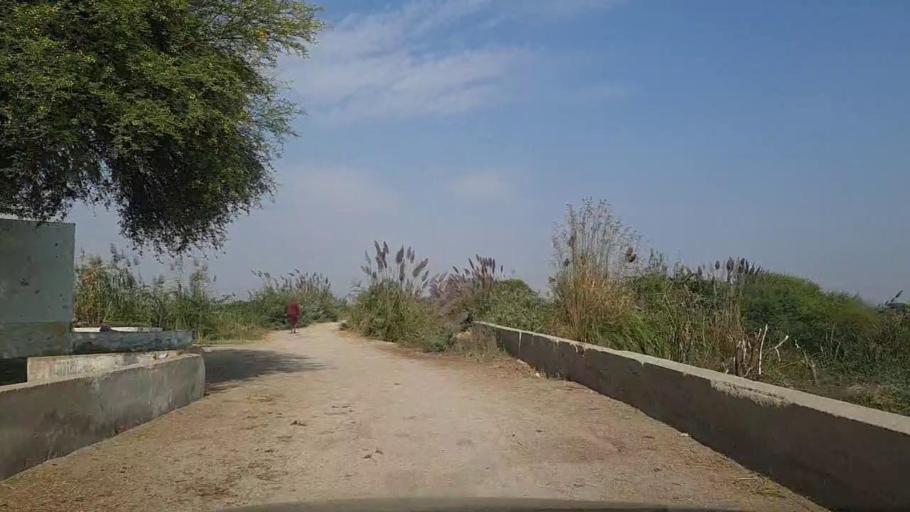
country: PK
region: Sindh
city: Thatta
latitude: 24.7631
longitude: 67.7681
